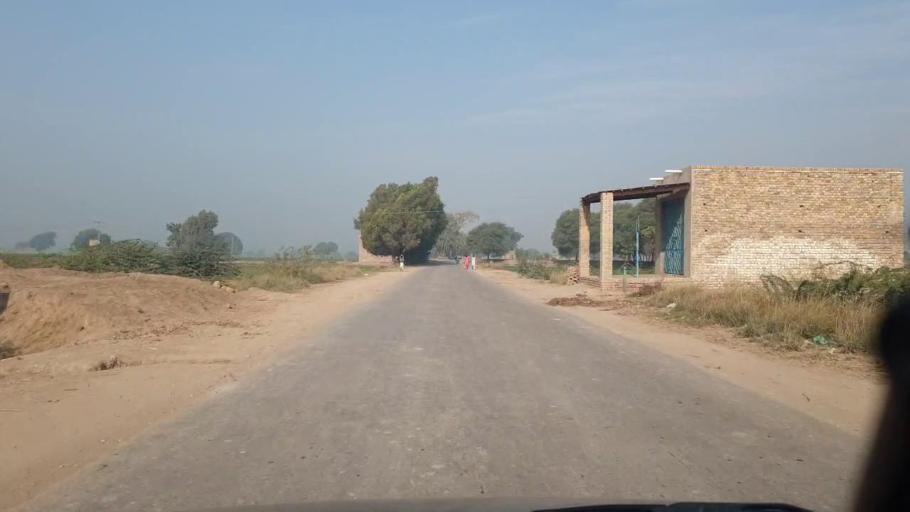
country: PK
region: Sindh
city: Shahdadpur
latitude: 25.9352
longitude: 68.6081
